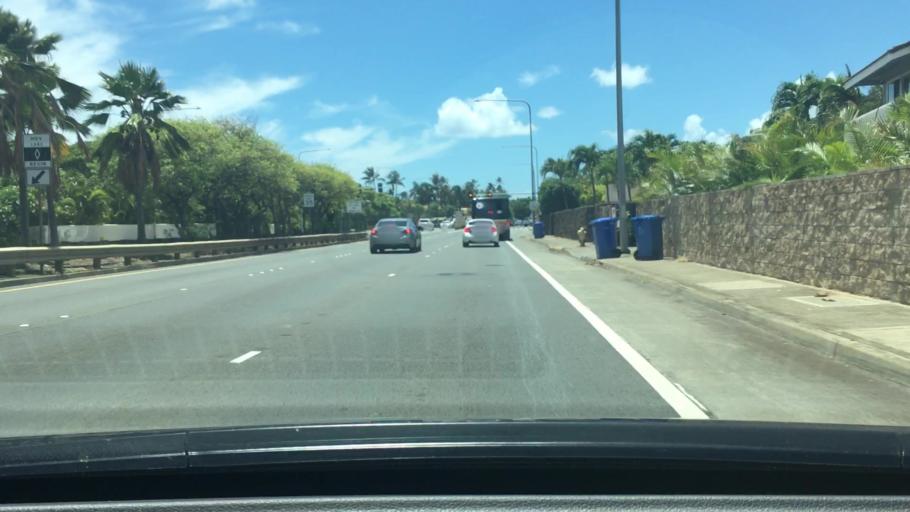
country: US
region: Hawaii
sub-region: Honolulu County
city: Waimanalo Beach
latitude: 21.2813
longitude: -157.7380
